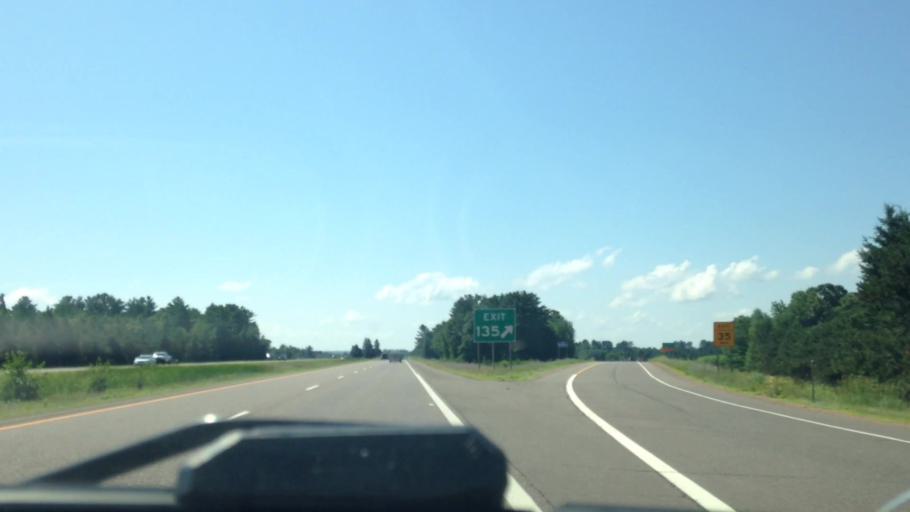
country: US
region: Wisconsin
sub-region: Barron County
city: Cameron
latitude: 45.4002
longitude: -91.7601
